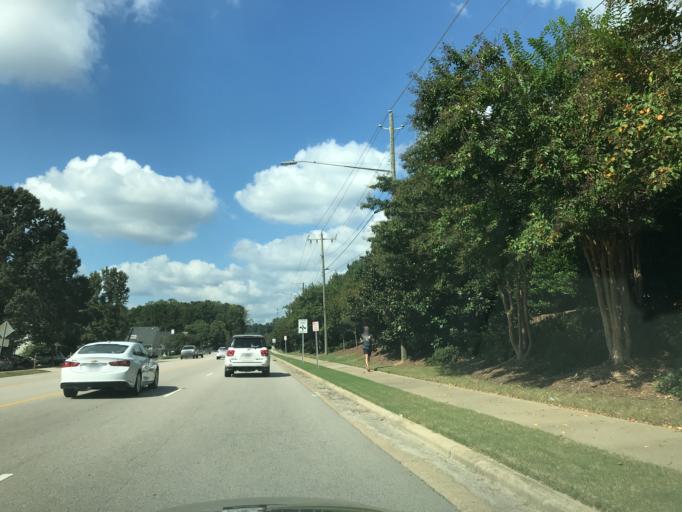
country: US
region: North Carolina
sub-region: Wake County
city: Wake Forest
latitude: 35.8870
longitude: -78.5544
